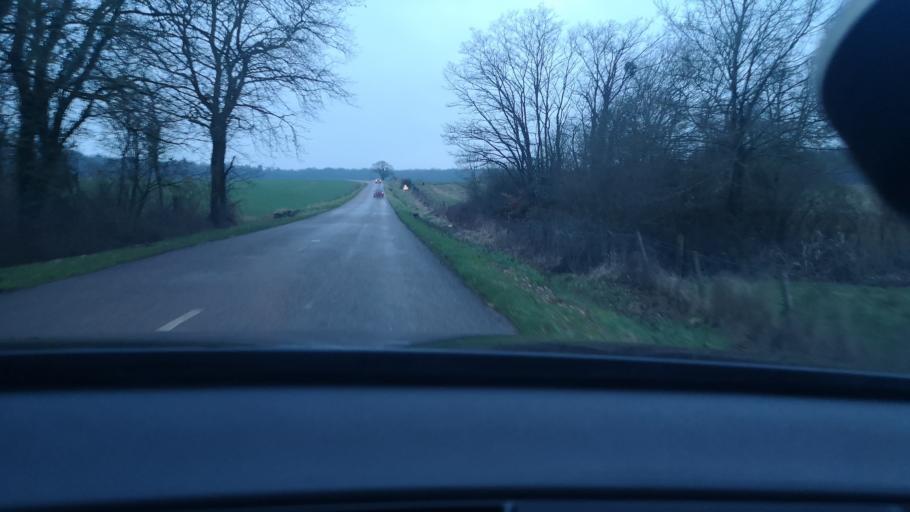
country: FR
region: Bourgogne
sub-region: Departement de la Cote-d'Or
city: Seurre
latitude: 47.0280
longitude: 5.0631
